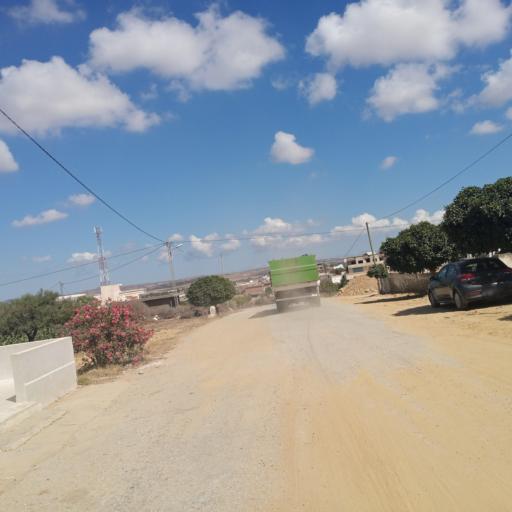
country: TN
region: Nabul
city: Qulaybiyah
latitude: 36.8563
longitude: 11.0353
